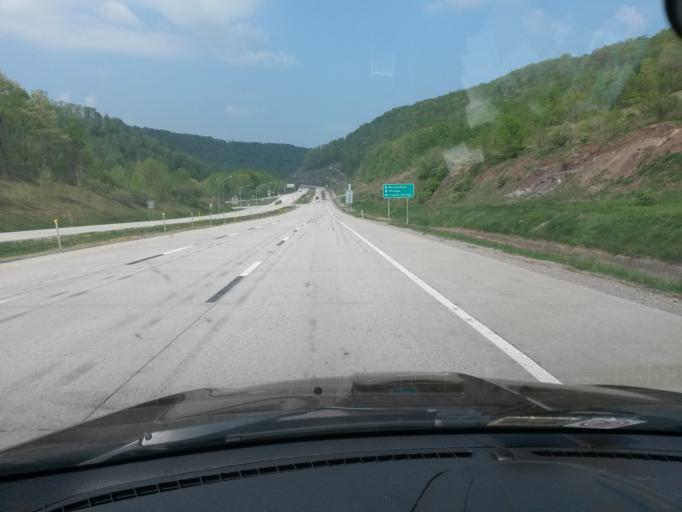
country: US
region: West Virginia
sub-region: Randolph County
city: Elkins
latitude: 38.9373
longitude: -79.9112
